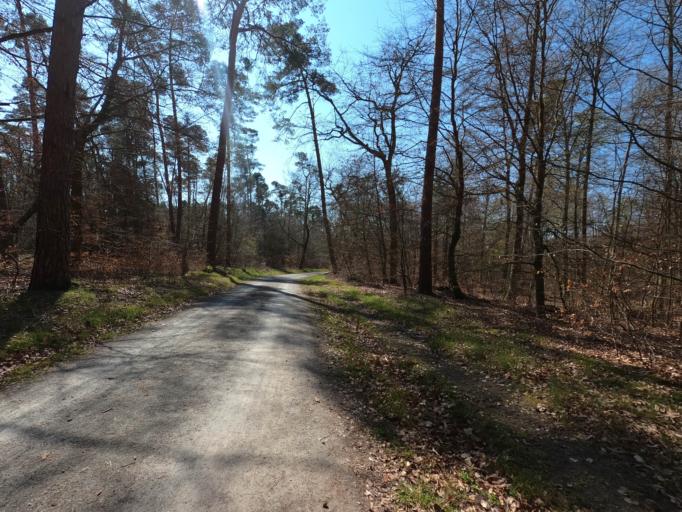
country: DE
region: Hesse
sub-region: Regierungsbezirk Darmstadt
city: Buttelborn
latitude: 49.9361
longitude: 8.5250
